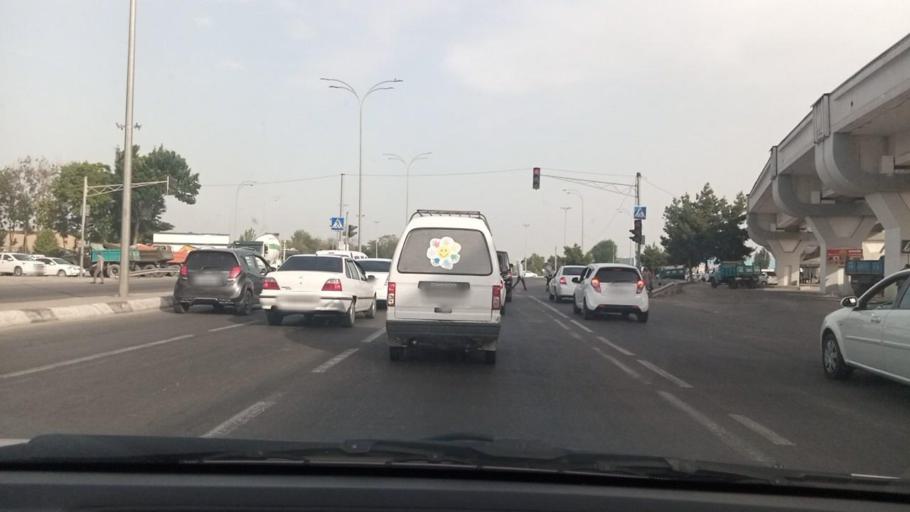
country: UZ
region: Toshkent Shahri
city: Bektemir
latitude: 41.2691
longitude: 69.3650
